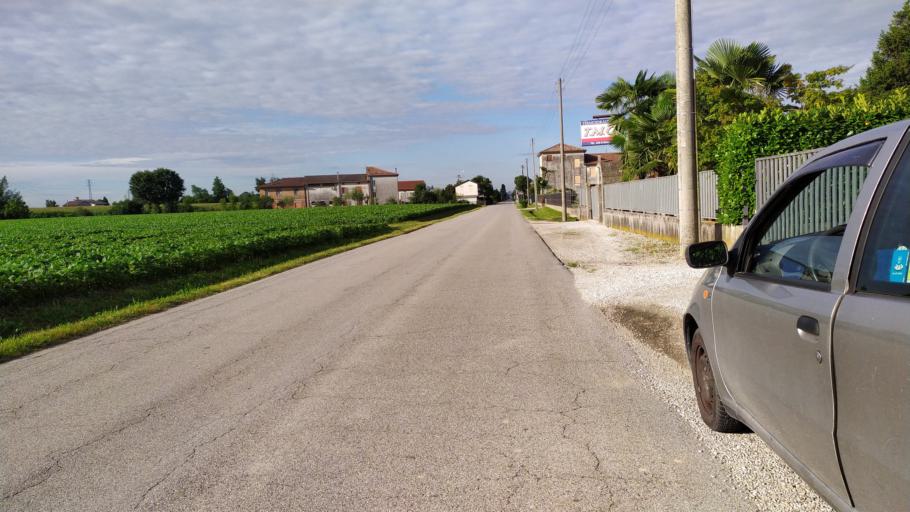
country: IT
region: Veneto
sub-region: Provincia di Padova
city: Abbazia Pisani
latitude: 45.6194
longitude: 11.8413
